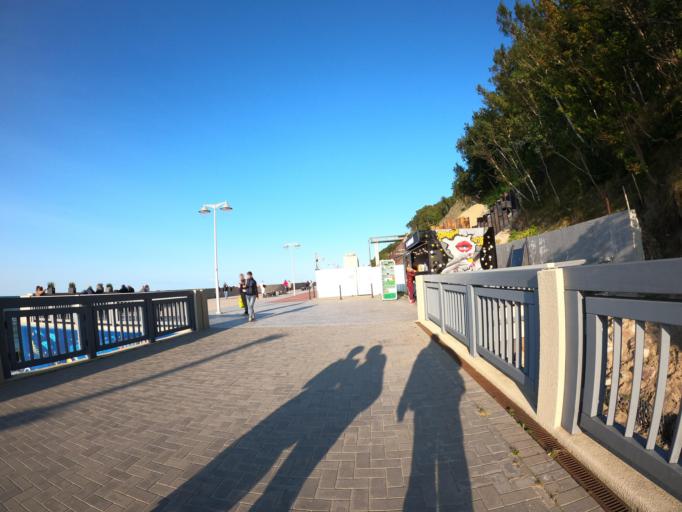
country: RU
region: Kaliningrad
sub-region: Gorod Svetlogorsk
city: Svetlogorsk
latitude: 54.9465
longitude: 20.1548
